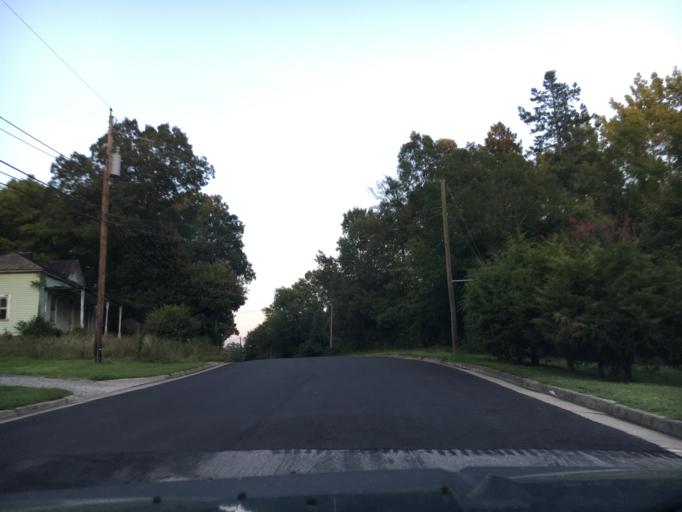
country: US
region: Virginia
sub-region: Halifax County
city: South Boston
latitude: 36.7092
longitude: -78.9040
